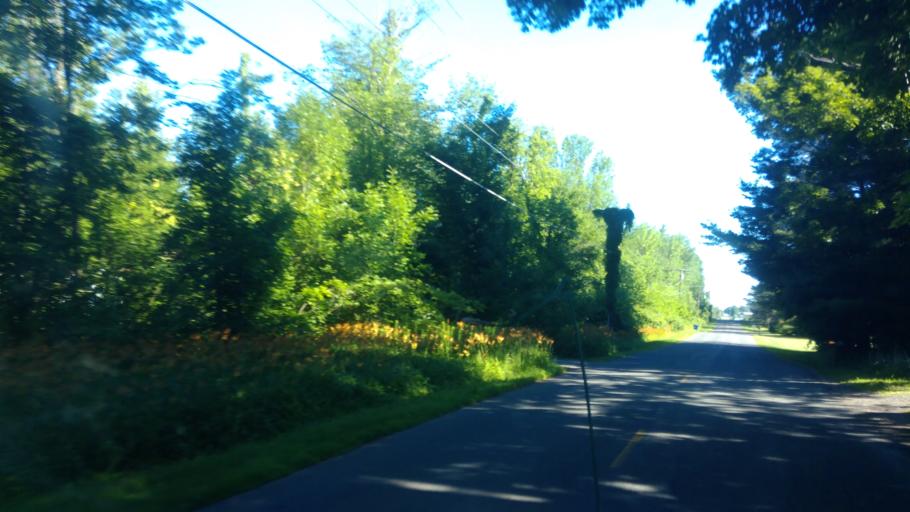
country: US
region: New York
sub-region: Wayne County
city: Sodus
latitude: 43.2661
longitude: -77.1128
